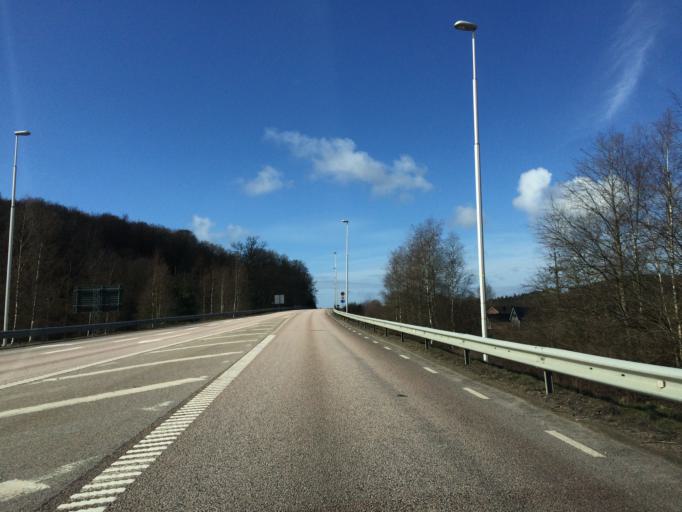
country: SE
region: Halland
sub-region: Laholms Kommun
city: Knared
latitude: 56.5126
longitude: 13.3217
